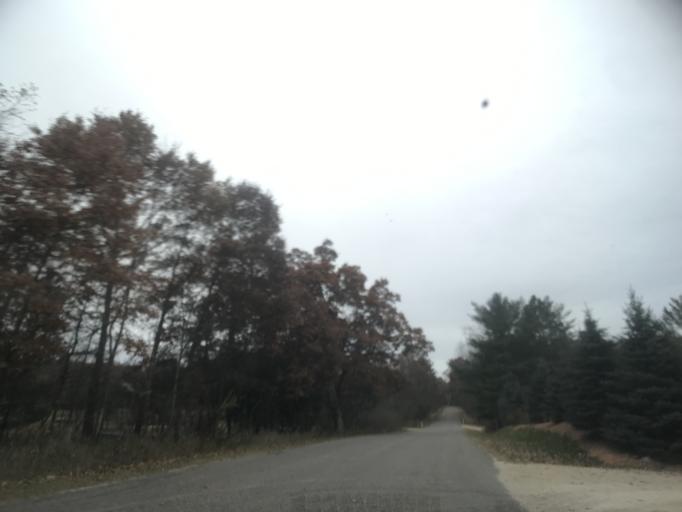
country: US
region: Michigan
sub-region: Dickinson County
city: Kingsford
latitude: 45.3819
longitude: -88.3211
